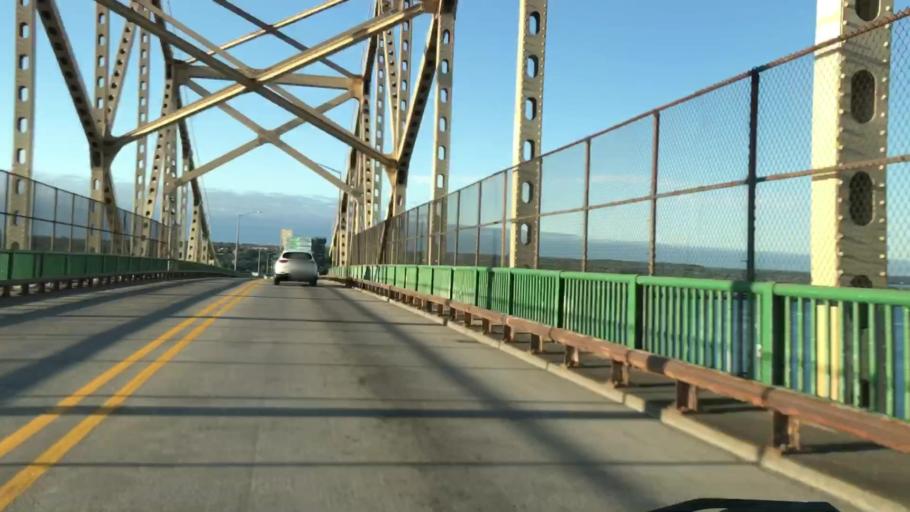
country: US
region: Michigan
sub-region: Chippewa County
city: Sault Ste. Marie
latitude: 46.5127
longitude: -84.3591
